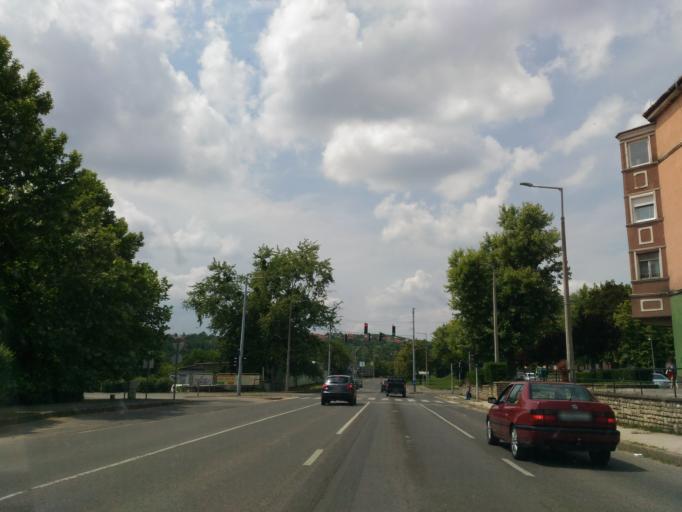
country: HU
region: Baranya
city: Komlo
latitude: 46.1928
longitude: 18.2570
